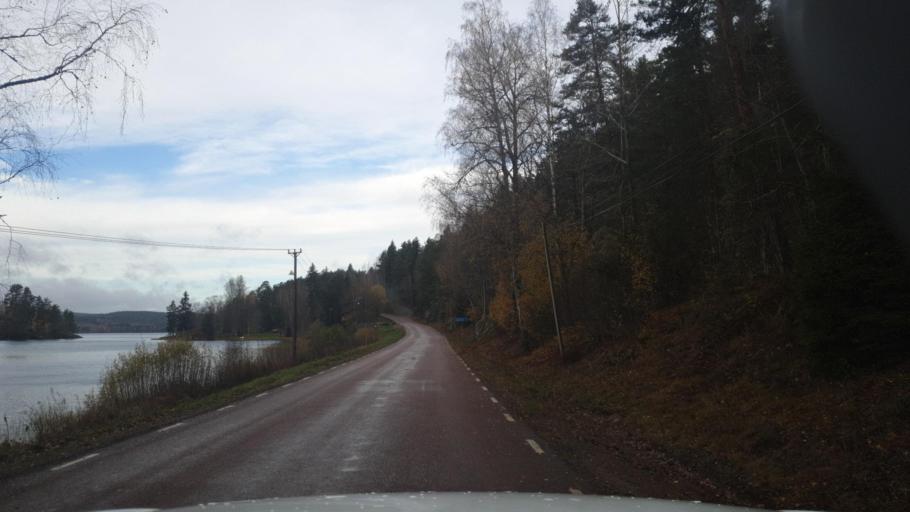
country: NO
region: Hedmark
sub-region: Eidskog
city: Skotterud
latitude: 59.8187
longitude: 12.0092
